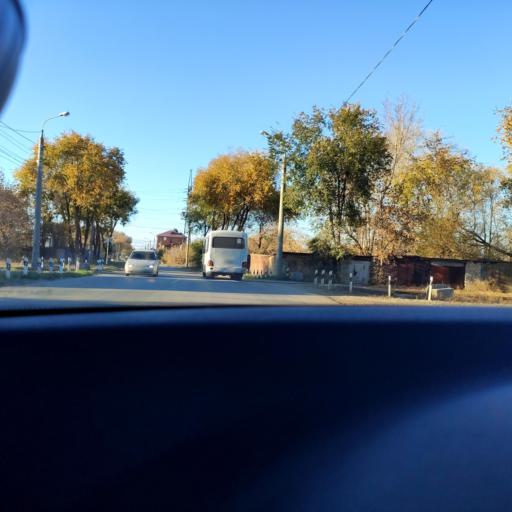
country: RU
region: Samara
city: Smyshlyayevka
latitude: 53.1911
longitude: 50.2771
